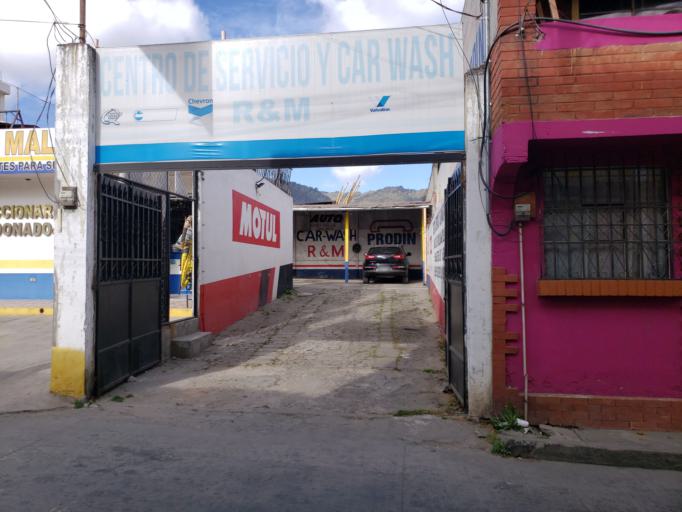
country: GT
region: Quetzaltenango
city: Ostuncalco
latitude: 14.8662
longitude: -91.6219
